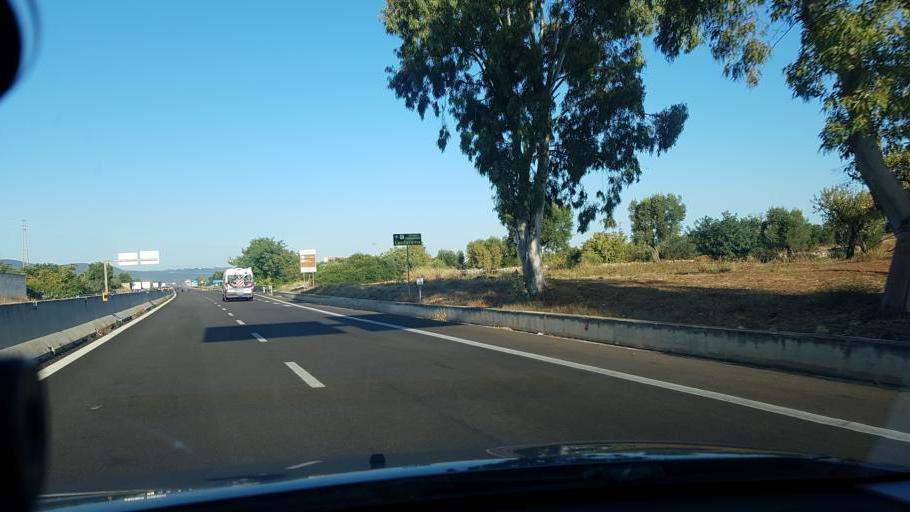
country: IT
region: Apulia
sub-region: Provincia di Brindisi
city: Fasano
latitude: 40.8365
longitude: 17.3851
